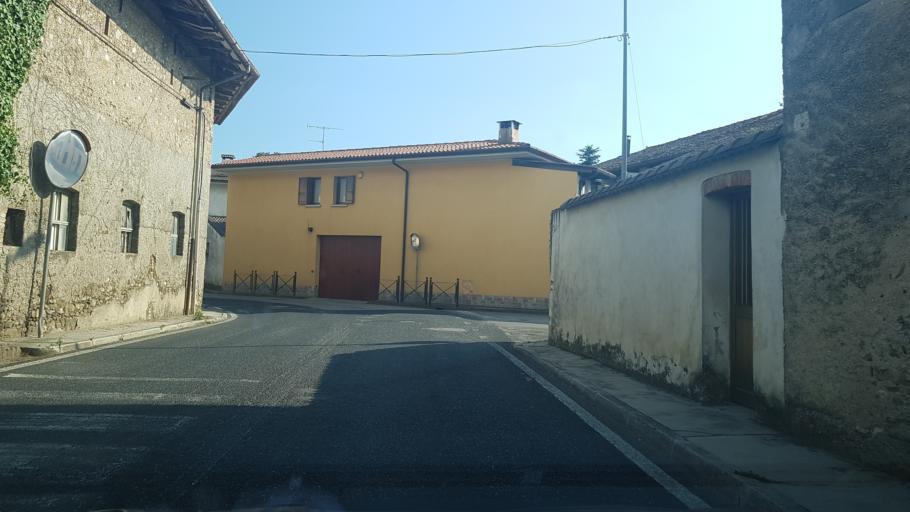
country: IT
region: Friuli Venezia Giulia
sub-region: Provincia di Udine
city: Basiliano-Vissandone
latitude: 46.0576
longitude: 13.0850
